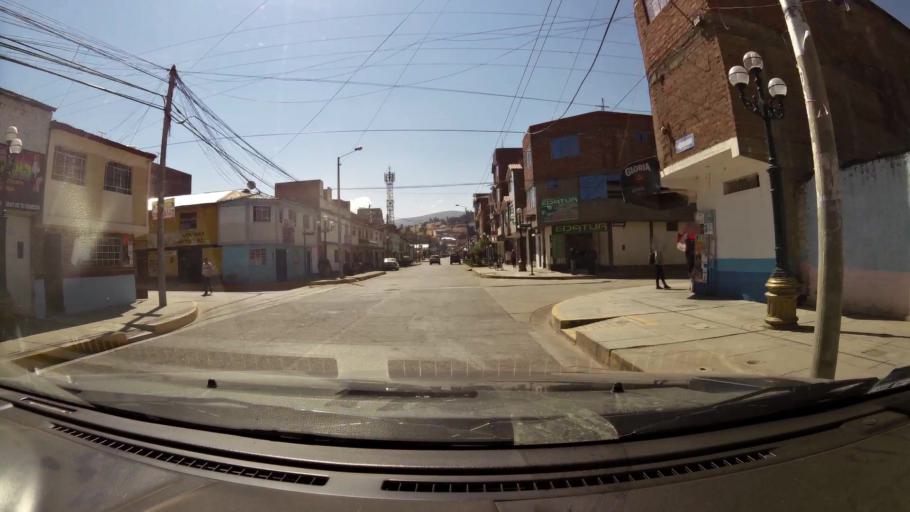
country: PE
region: Junin
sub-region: Provincia de Concepcion
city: Concepcion
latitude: -11.9201
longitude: -75.3155
